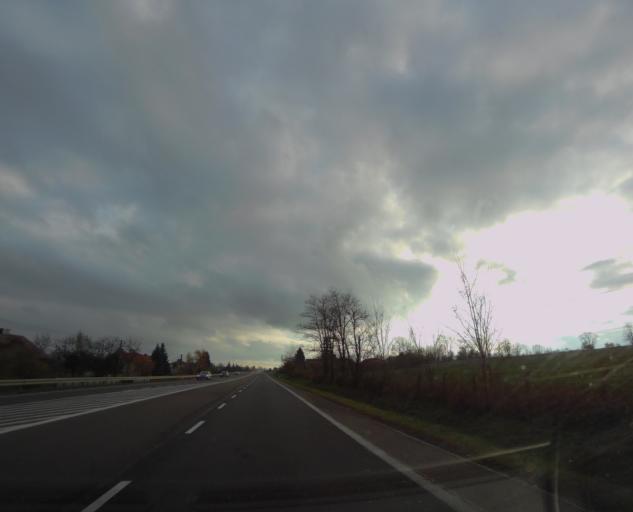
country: PL
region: Subcarpathian Voivodeship
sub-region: Powiat przemyski
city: Orly
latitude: 49.8984
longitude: 22.8164
